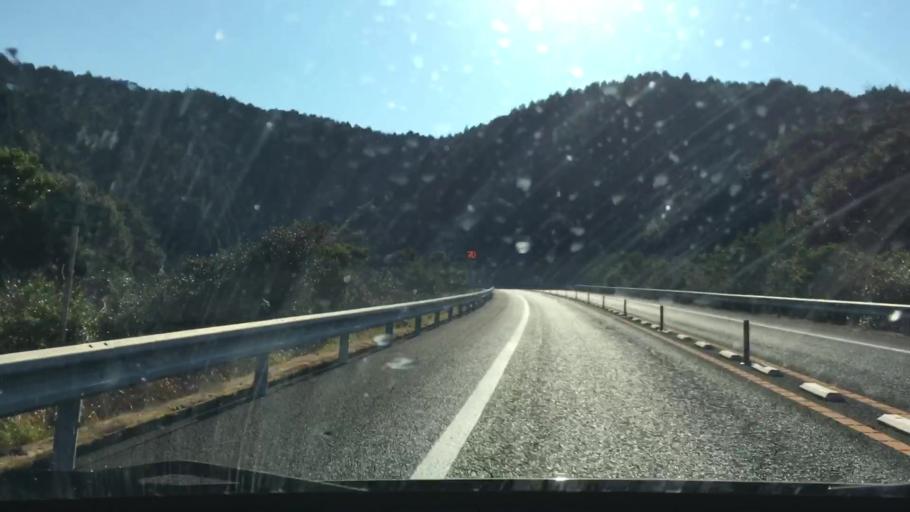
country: JP
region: Kagoshima
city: Kokubu-matsuki
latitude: 31.7267
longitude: 130.8407
